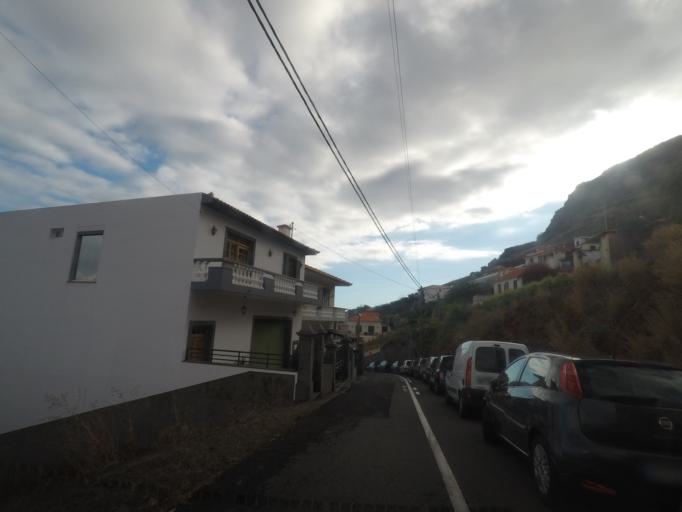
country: PT
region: Madeira
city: Camara de Lobos
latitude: 32.6542
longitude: -16.9918
